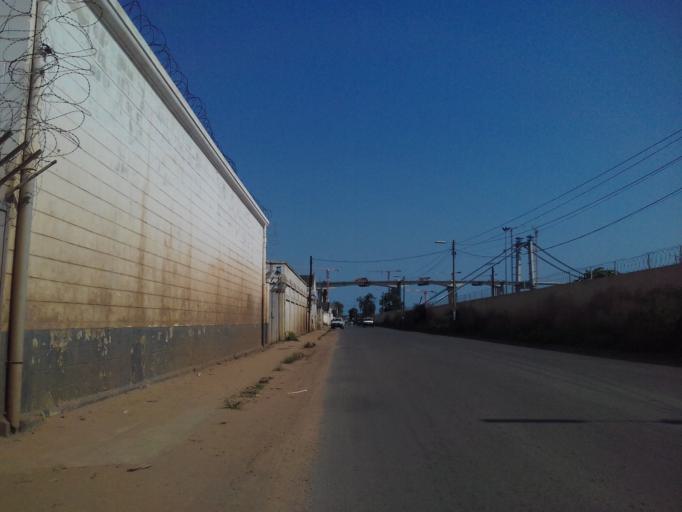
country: MZ
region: Maputo City
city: Maputo
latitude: -25.9600
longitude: 32.5553
